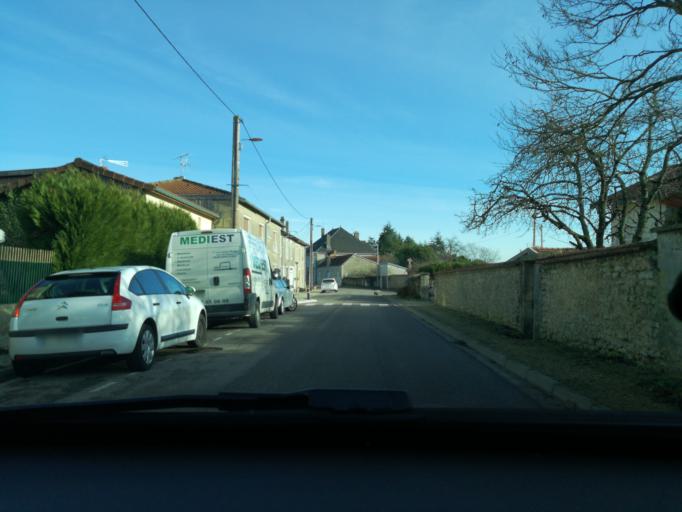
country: FR
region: Lorraine
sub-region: Departement de la Meuse
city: Fains-Veel
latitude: 48.8137
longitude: 5.0878
